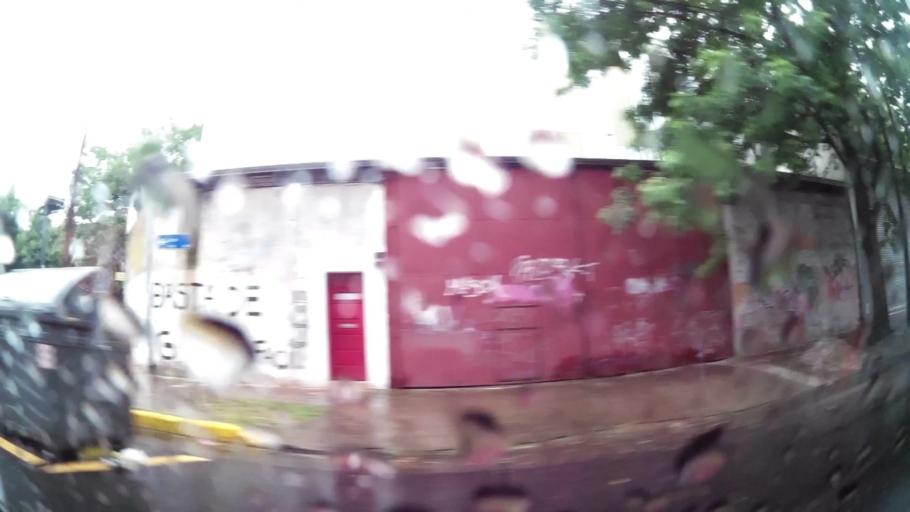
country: AR
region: Buenos Aires
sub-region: Partido de Avellaneda
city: Avellaneda
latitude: -34.6443
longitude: -58.3656
